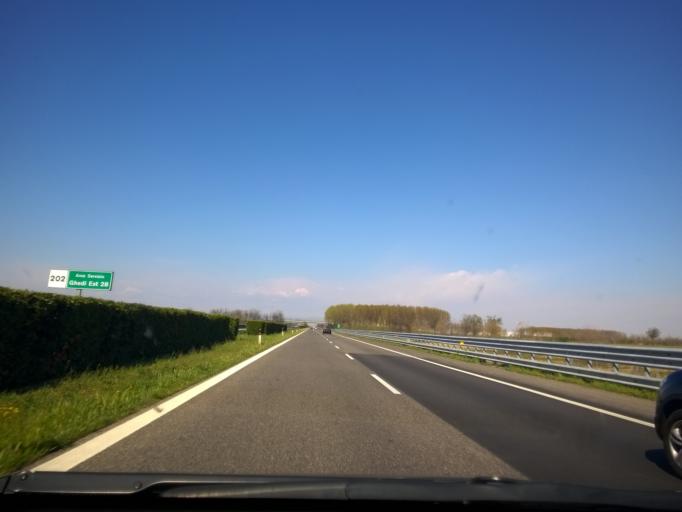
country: IT
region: Lombardy
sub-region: Provincia di Cremona
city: Corte de' Frati
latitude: 45.2037
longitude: 10.1030
